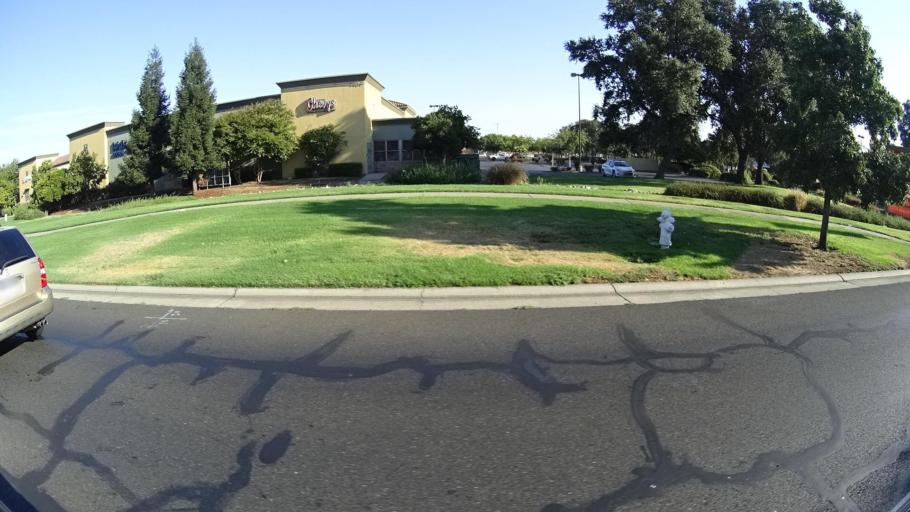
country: US
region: California
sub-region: Sacramento County
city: Laguna
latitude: 38.4238
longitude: -121.4161
